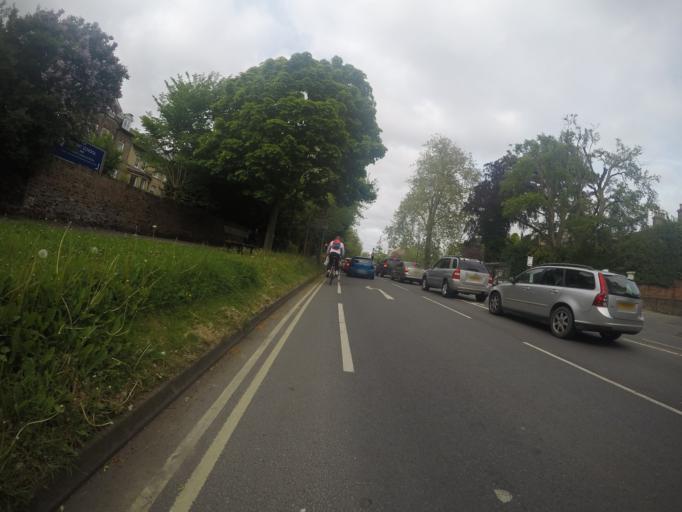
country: GB
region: England
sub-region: City of York
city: York
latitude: 53.9515
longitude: -1.0973
